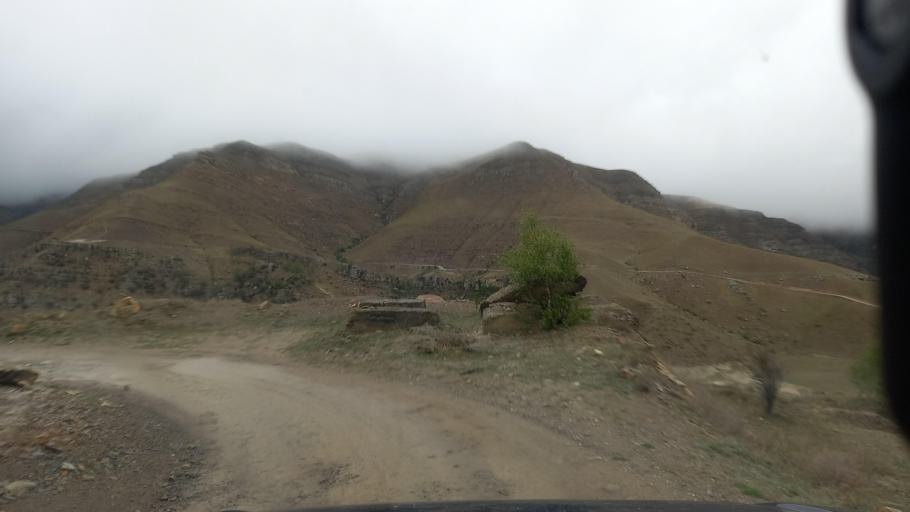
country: RU
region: Kabardino-Balkariya
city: Bylym
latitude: 43.4613
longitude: 42.9912
